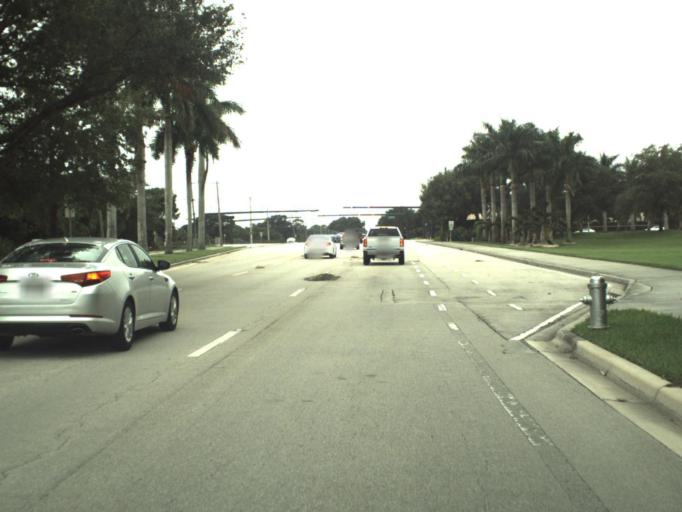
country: US
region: Florida
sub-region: Palm Beach County
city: Kings Point
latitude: 26.3960
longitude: -80.1215
